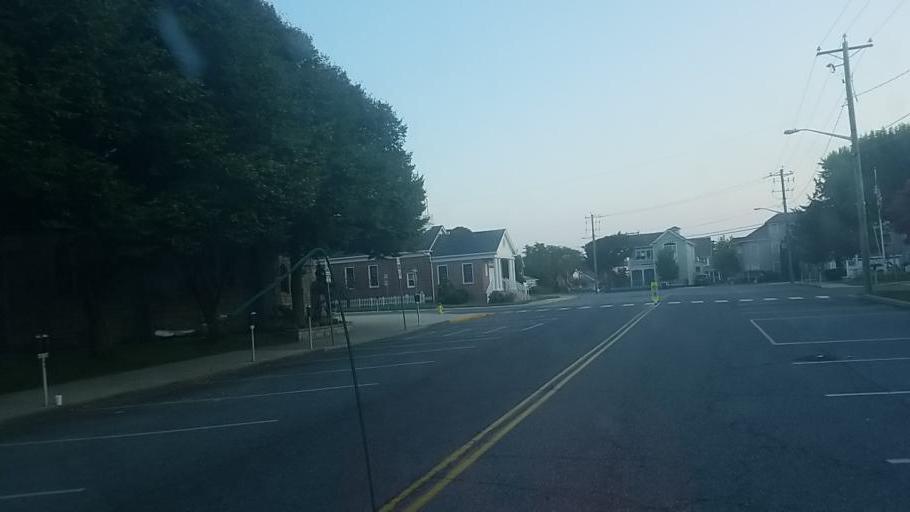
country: US
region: Delaware
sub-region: Sussex County
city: Rehoboth Beach
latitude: 38.7127
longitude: -75.0782
